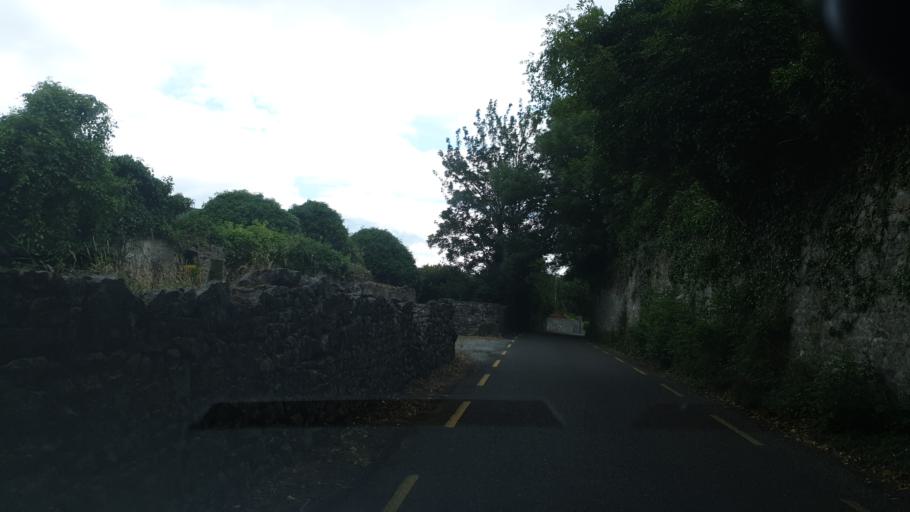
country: IE
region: Munster
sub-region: Ciarrai
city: Tralee
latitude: 52.2536
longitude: -9.6434
